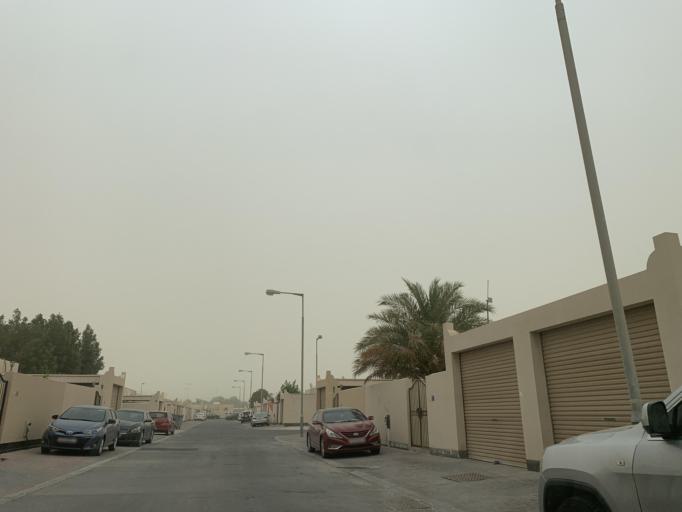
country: BH
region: Central Governorate
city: Madinat Hamad
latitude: 26.1336
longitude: 50.5246
